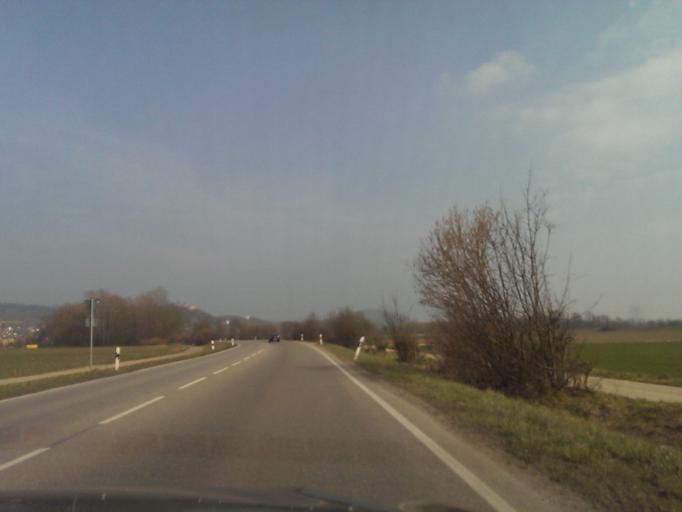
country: DE
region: Bavaria
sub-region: Upper Palatinate
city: Tegernheim
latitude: 49.0254
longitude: 12.1837
